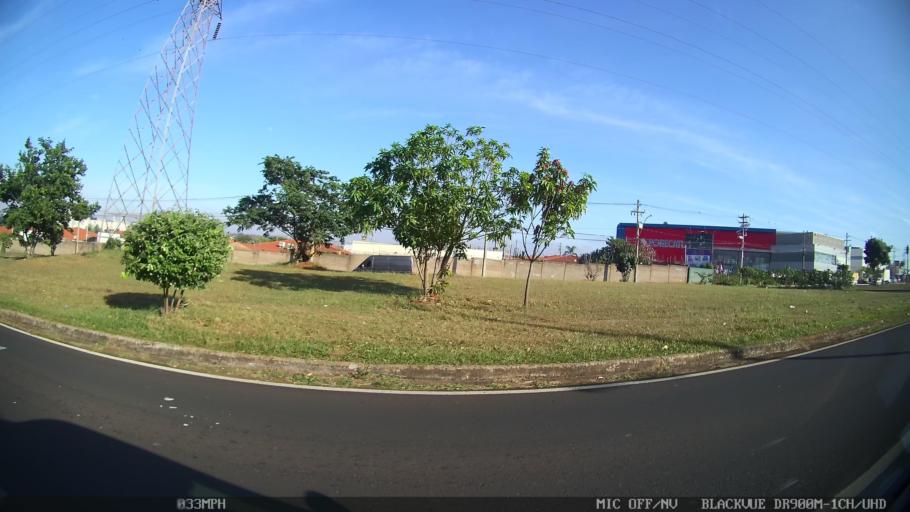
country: BR
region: Sao Paulo
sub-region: Sao Jose Do Rio Preto
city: Sao Jose do Rio Preto
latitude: -20.7810
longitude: -49.3428
